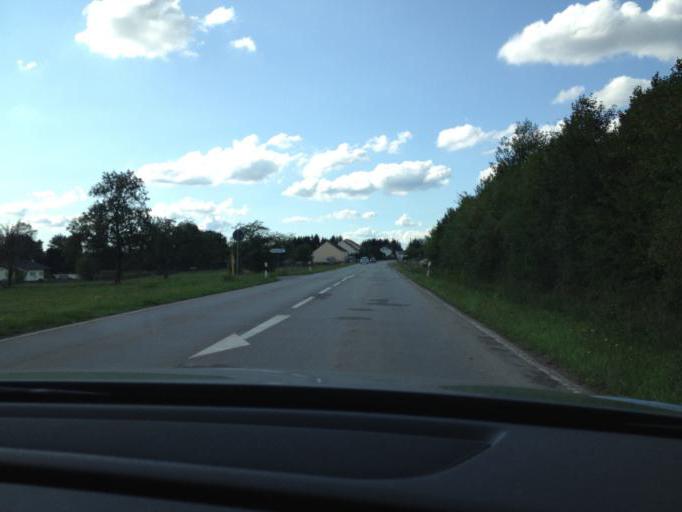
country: DE
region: Saarland
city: Losheim
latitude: 49.5022
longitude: 6.7887
